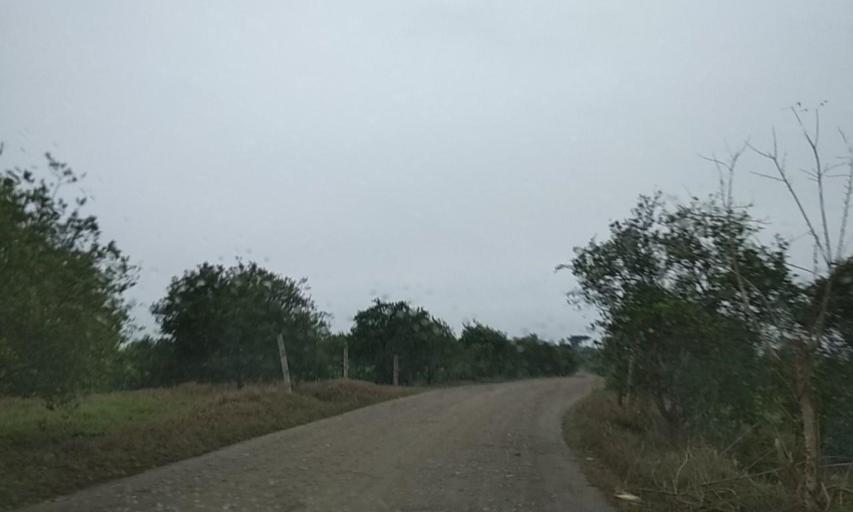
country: MX
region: Veracruz
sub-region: Papantla
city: El Chote
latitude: 20.3366
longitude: -97.3903
